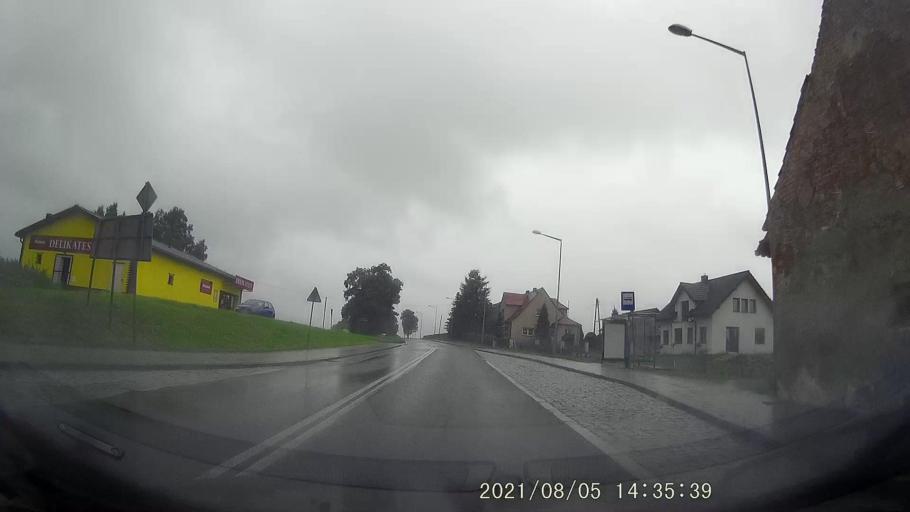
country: PL
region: Opole Voivodeship
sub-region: Powiat nyski
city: Lambinowice
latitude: 50.4673
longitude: 17.4997
